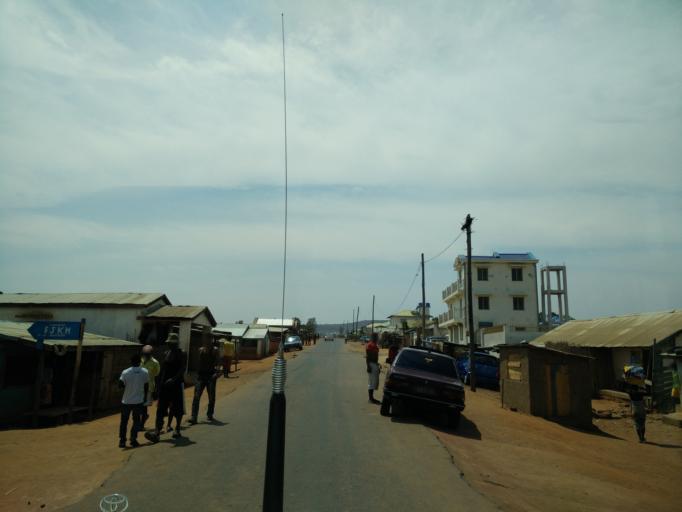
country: MG
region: Ihorombe
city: Ranohira
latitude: -22.7719
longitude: 45.1073
